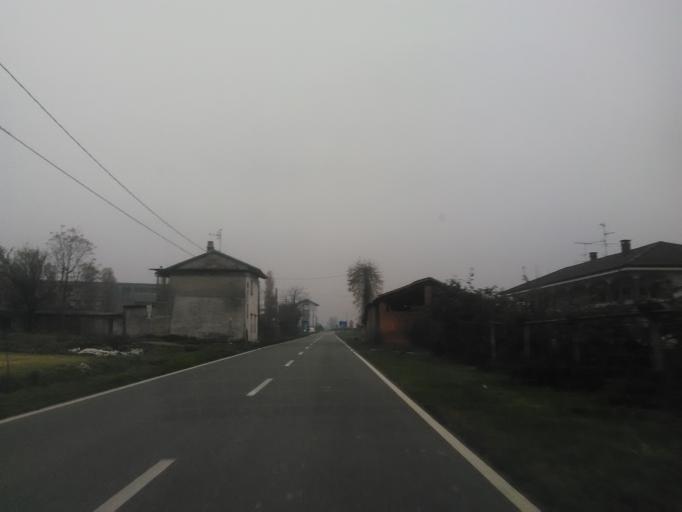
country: IT
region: Piedmont
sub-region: Provincia di Vercelli
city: Cigliano
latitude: 45.3195
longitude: 8.0207
